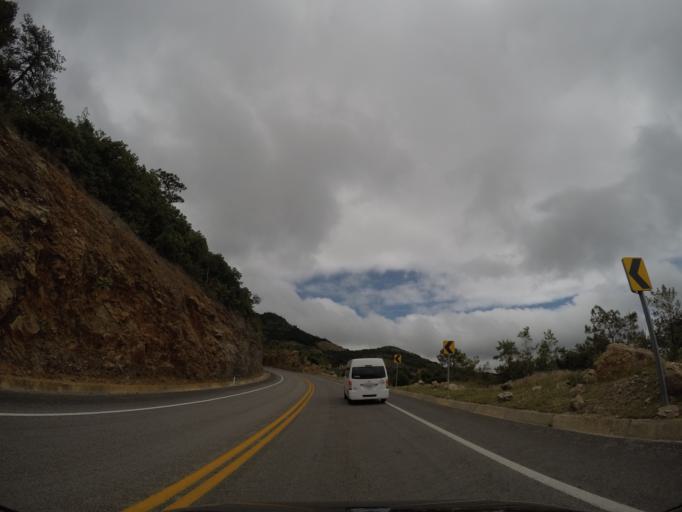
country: MX
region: Oaxaca
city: San Lorenzo Albarradas
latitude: 16.9293
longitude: -96.2612
